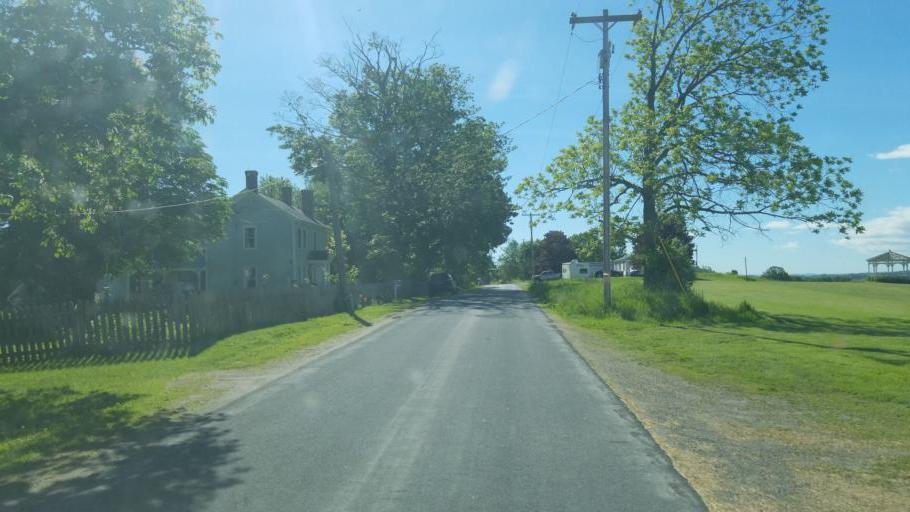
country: US
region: New York
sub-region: Montgomery County
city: Fort Plain
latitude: 42.9152
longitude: -74.6274
